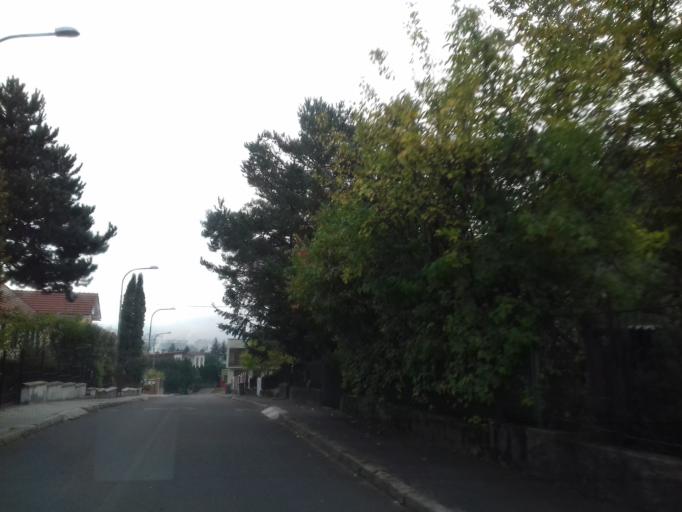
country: SK
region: Banskobystricky
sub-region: Okres Banska Bystrica
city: Banska Bystrica
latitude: 48.7538
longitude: 19.1533
